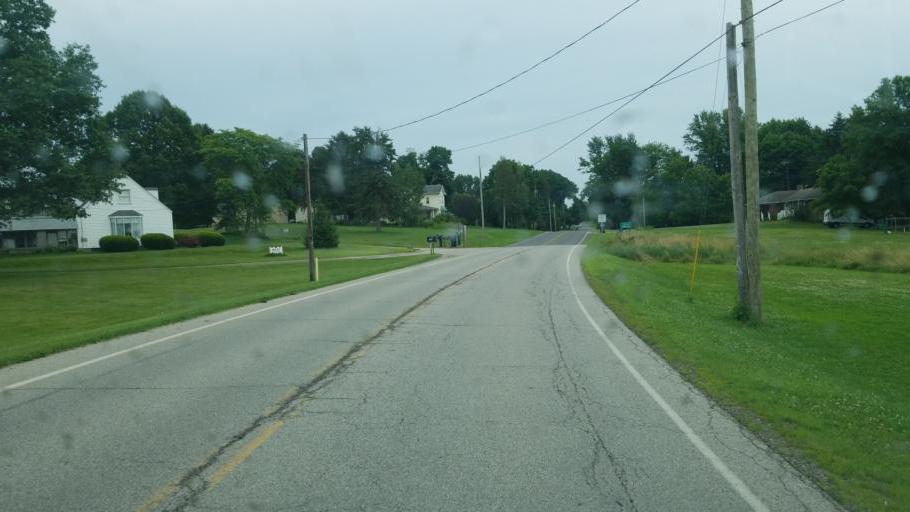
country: US
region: Ohio
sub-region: Summit County
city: Clinton
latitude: 40.9139
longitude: -81.6255
